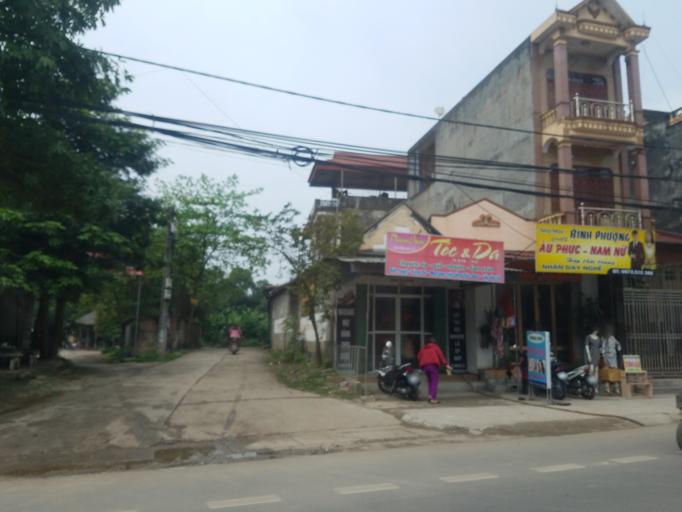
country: VN
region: Thai Nguyen
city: Chua Hang
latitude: 21.6111
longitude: 105.8398
